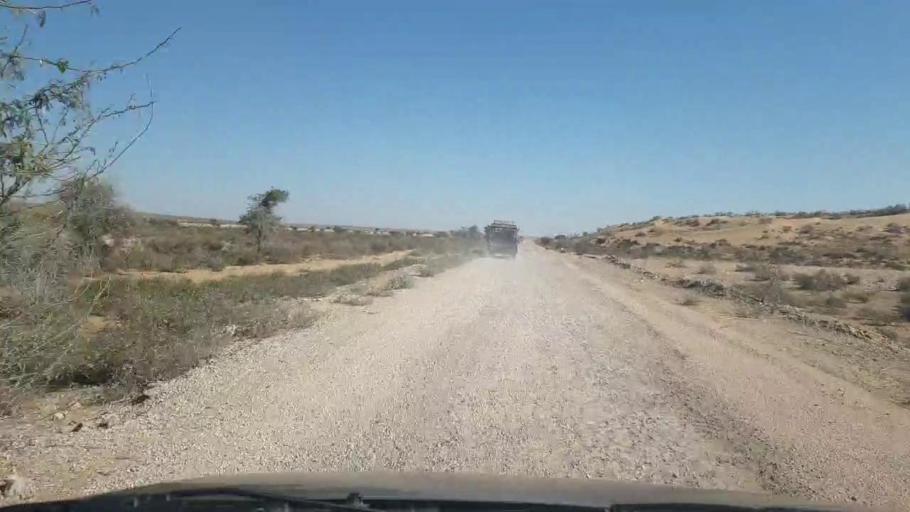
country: PK
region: Sindh
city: Bozdar
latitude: 27.0147
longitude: 68.7462
